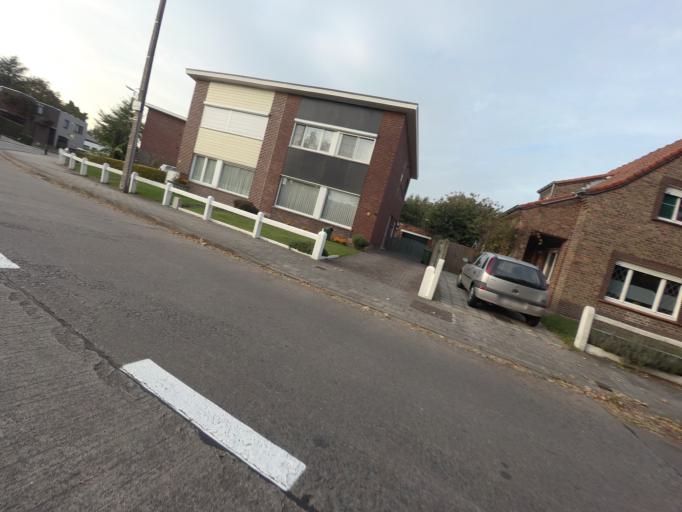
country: BE
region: Flanders
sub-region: Provincie Oost-Vlaanderen
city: Destelbergen
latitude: 51.0739
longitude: 3.7692
